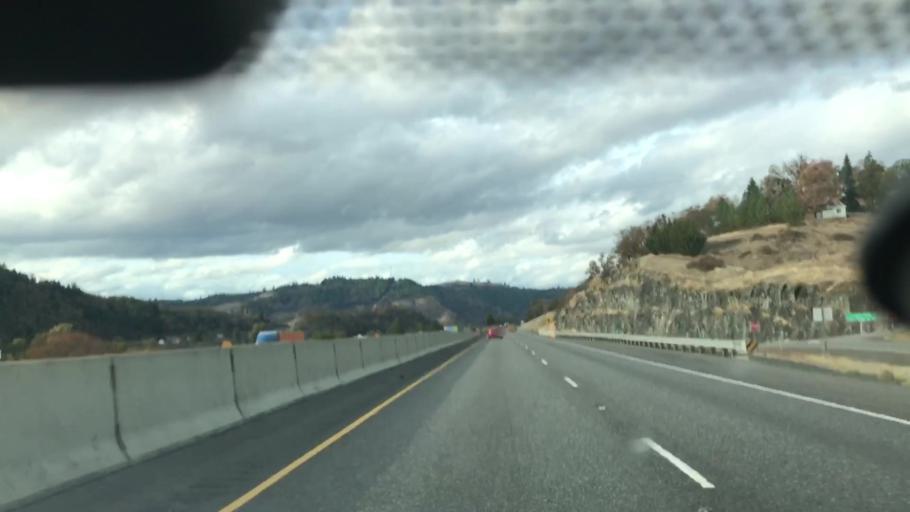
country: US
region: Oregon
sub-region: Douglas County
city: Winston
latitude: 43.0731
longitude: -123.3568
